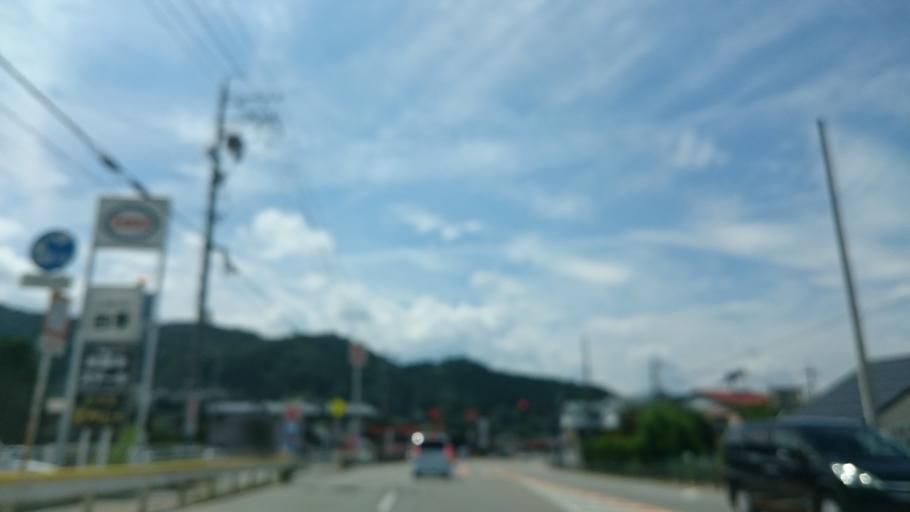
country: JP
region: Gifu
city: Takayama
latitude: 36.1287
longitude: 137.2521
